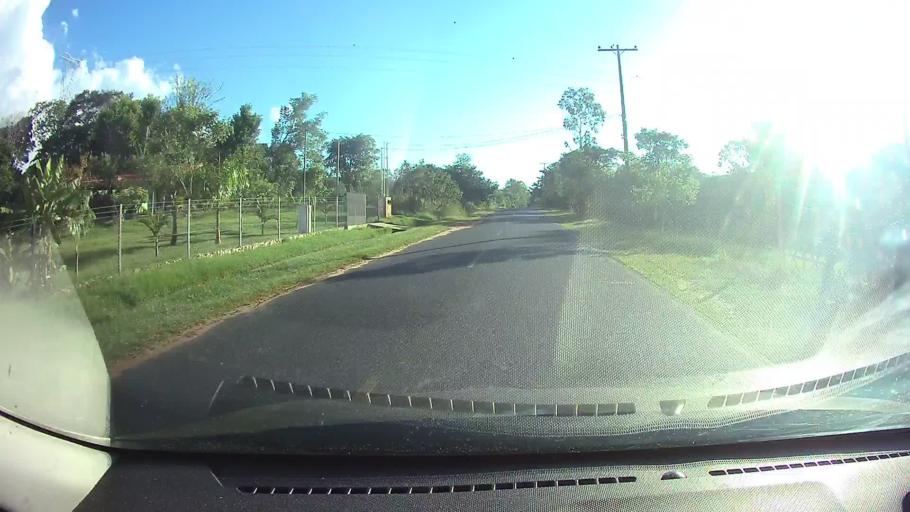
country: PY
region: Cordillera
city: Emboscada
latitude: -25.1794
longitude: -57.2922
